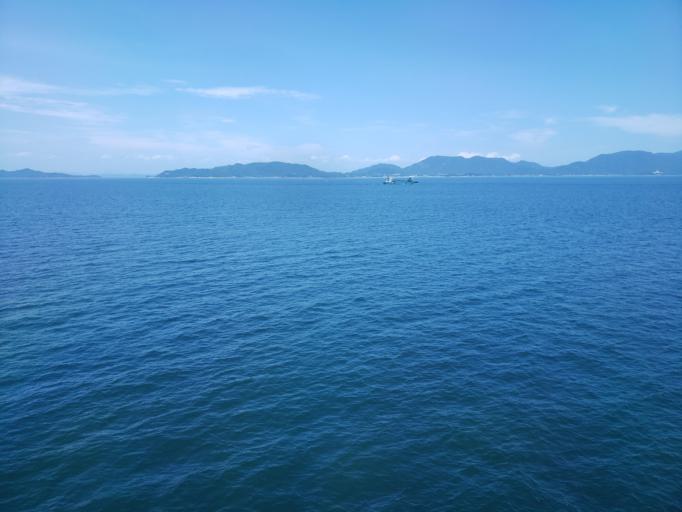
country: JP
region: Kagawa
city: Tonosho
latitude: 34.4064
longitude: 134.1735
